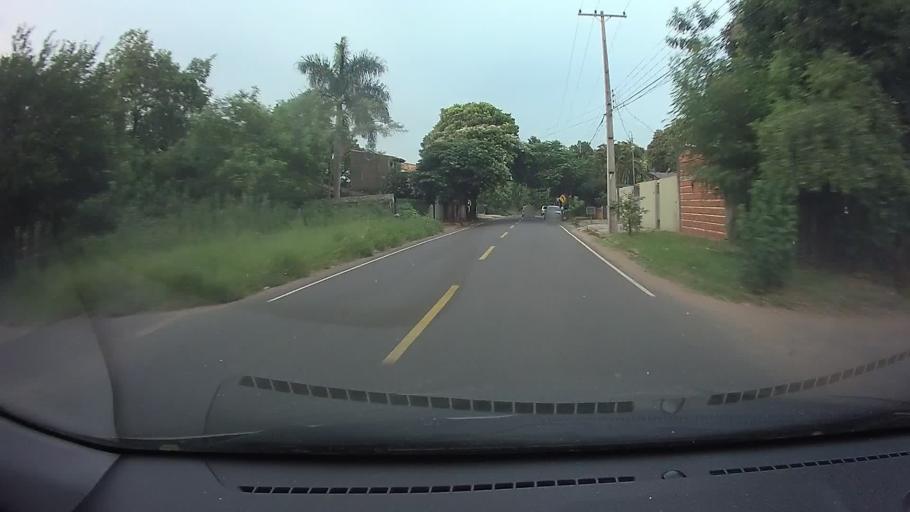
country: PY
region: Central
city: San Lorenzo
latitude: -25.2576
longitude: -57.5032
